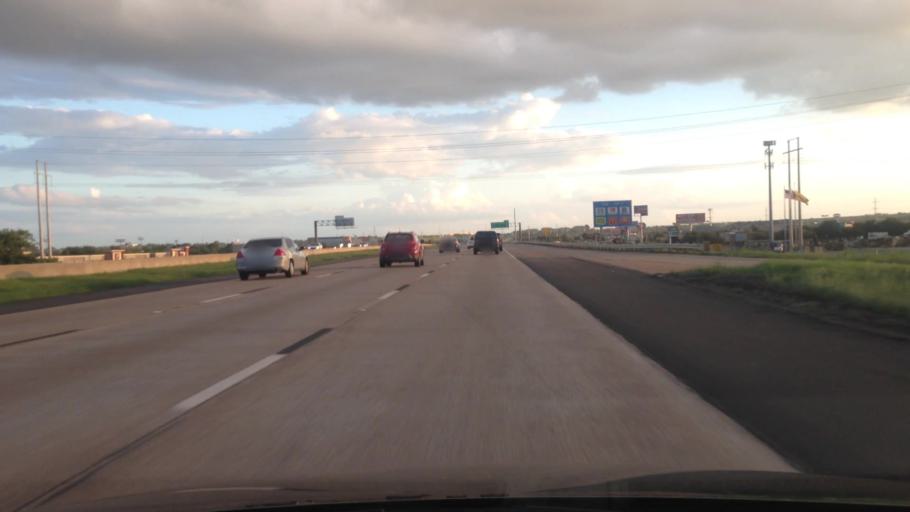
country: US
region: Texas
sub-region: Tarrant County
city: White Settlement
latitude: 32.7698
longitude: -97.4762
